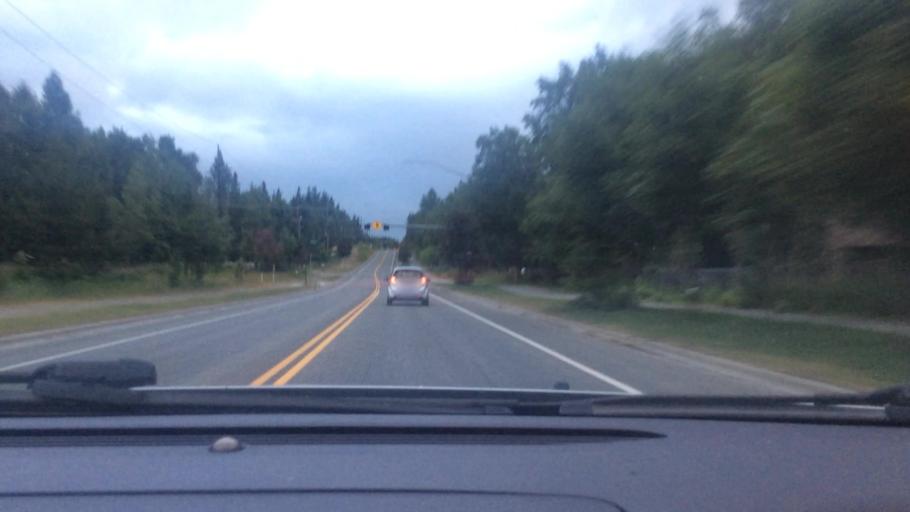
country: US
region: Alaska
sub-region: Anchorage Municipality
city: Anchorage
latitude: 61.1458
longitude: -149.8043
